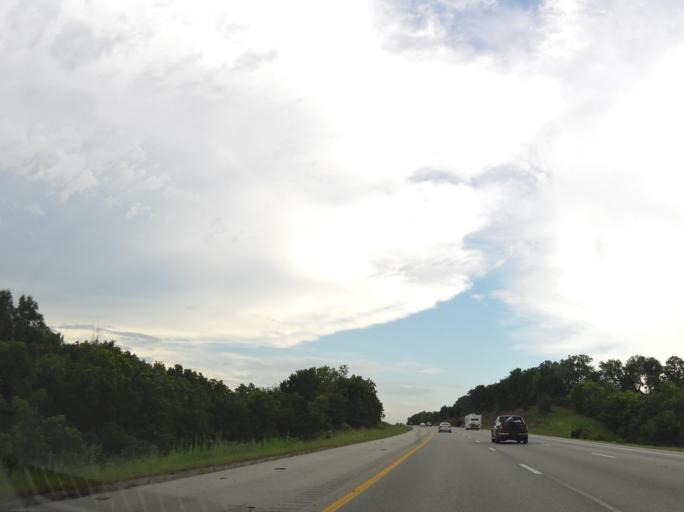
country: US
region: Kentucky
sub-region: Madison County
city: Berea
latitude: 37.6506
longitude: -84.3122
